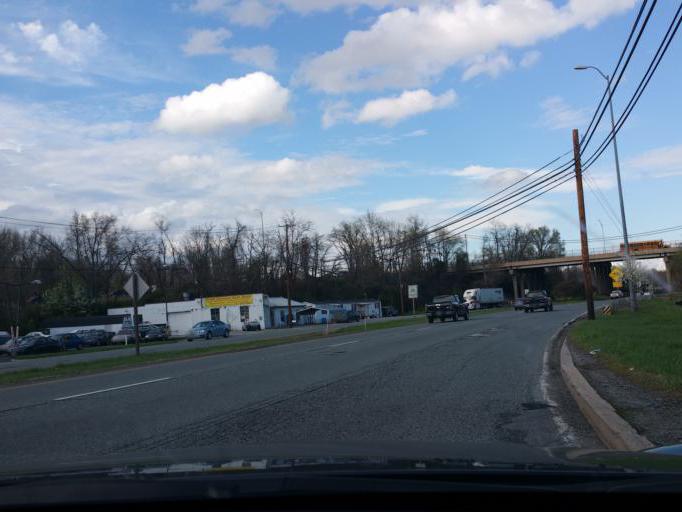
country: US
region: Maryland
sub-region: Harford County
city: Aberdeen
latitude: 39.5143
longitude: -76.1600
